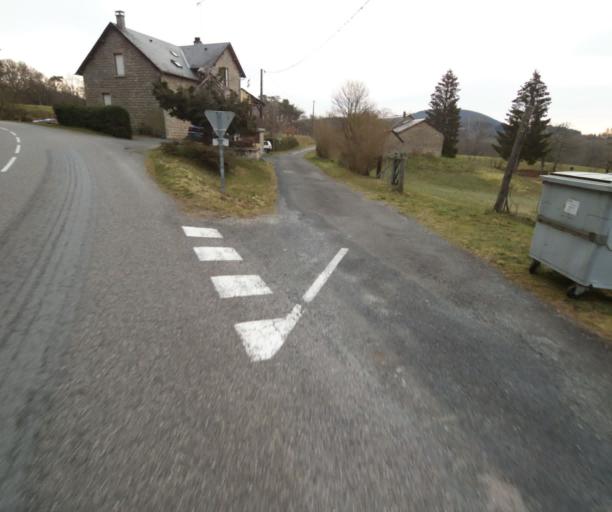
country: FR
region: Limousin
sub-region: Departement de la Correze
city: Correze
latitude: 45.4283
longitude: 1.8496
